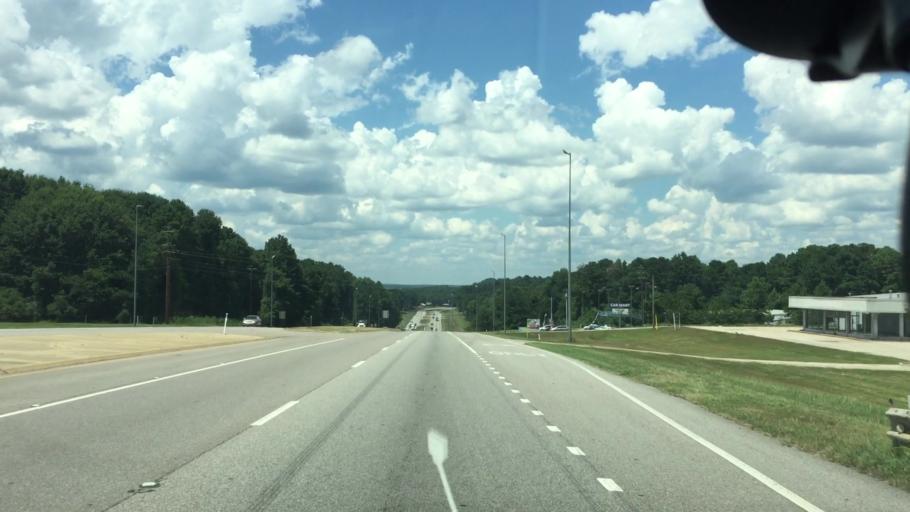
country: US
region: Alabama
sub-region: Pike County
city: Troy
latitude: 31.8118
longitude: -85.9909
